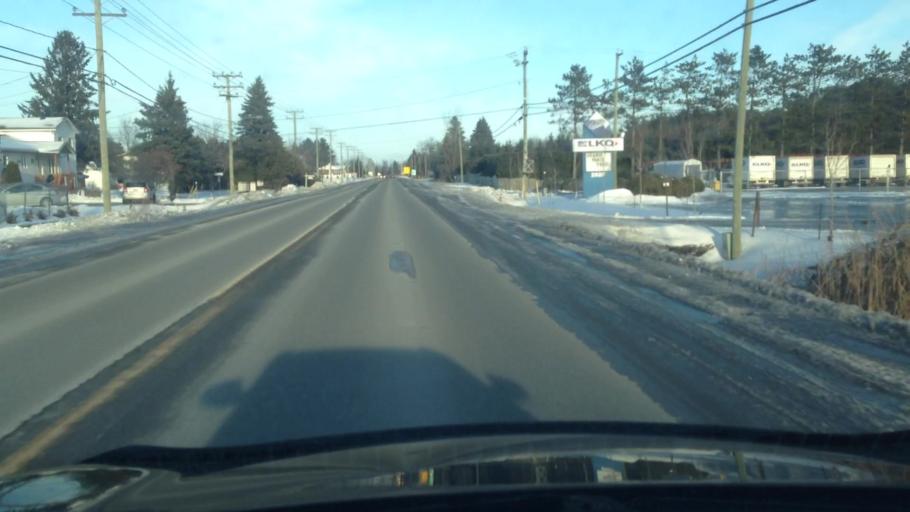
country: CA
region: Quebec
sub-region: Laurentides
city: Sainte-Sophie
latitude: 45.7914
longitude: -73.9448
